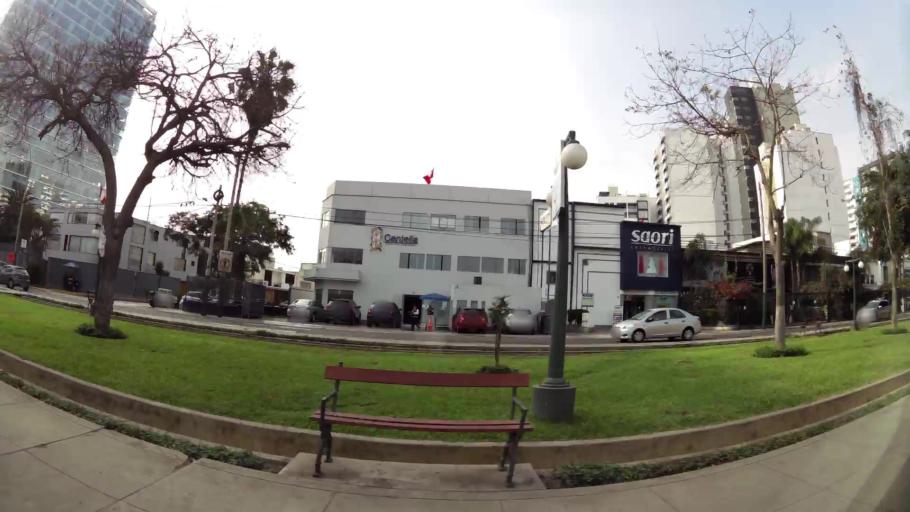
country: PE
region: Lima
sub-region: Lima
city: San Isidro
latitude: -12.0934
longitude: -77.0604
